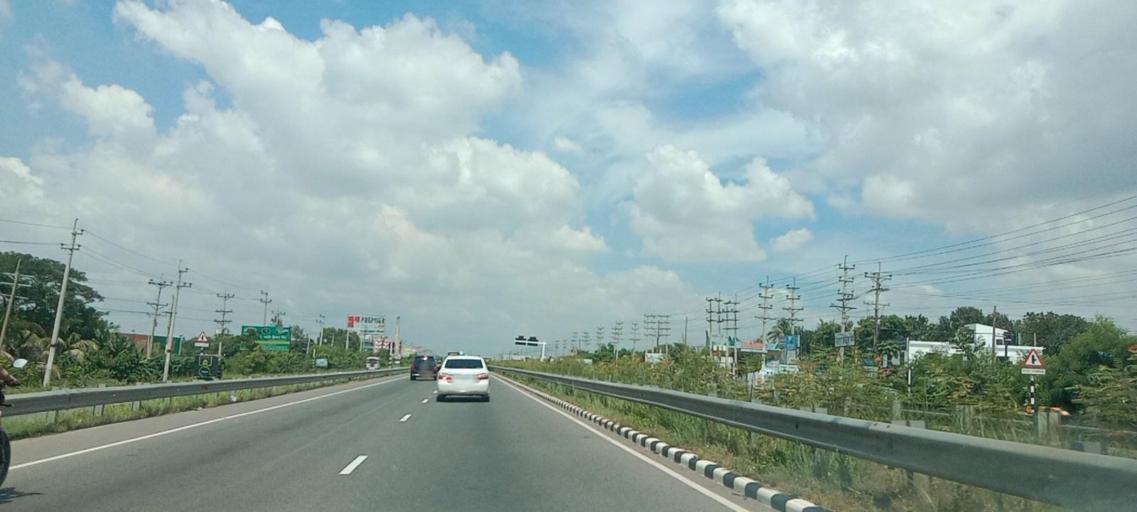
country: BD
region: Dhaka
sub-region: Dhaka
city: Dhaka
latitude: 23.6619
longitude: 90.3764
